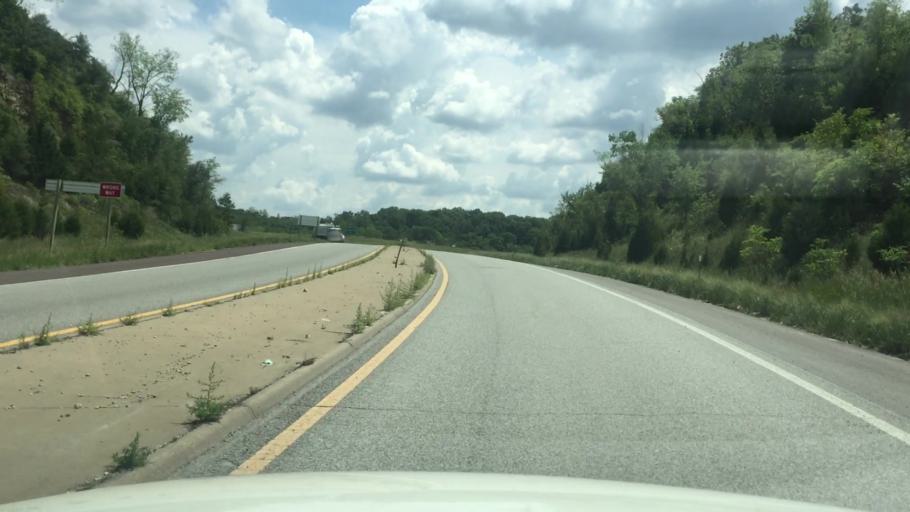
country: US
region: Kansas
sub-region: Wyandotte County
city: Edwardsville
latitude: 39.0410
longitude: -94.7921
